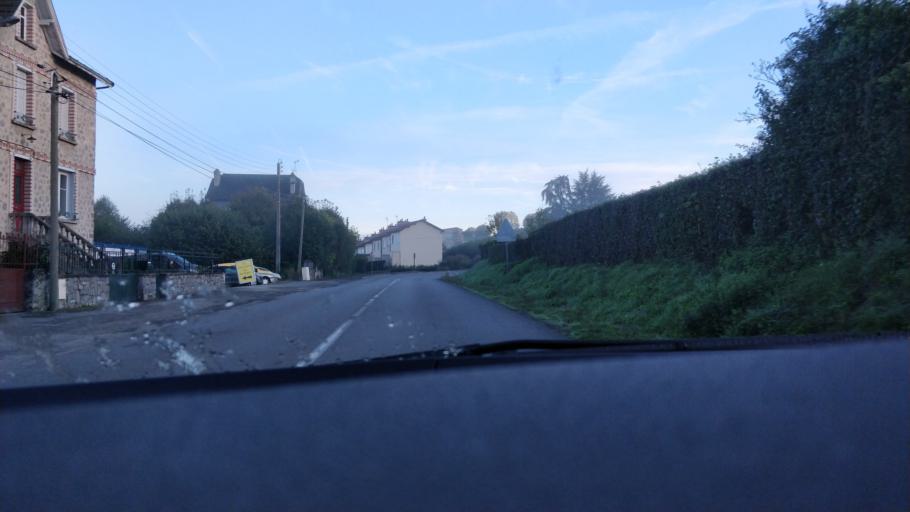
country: FR
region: Limousin
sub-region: Departement de la Haute-Vienne
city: Saint-Leonard-de-Noblat
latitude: 45.8307
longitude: 1.4842
